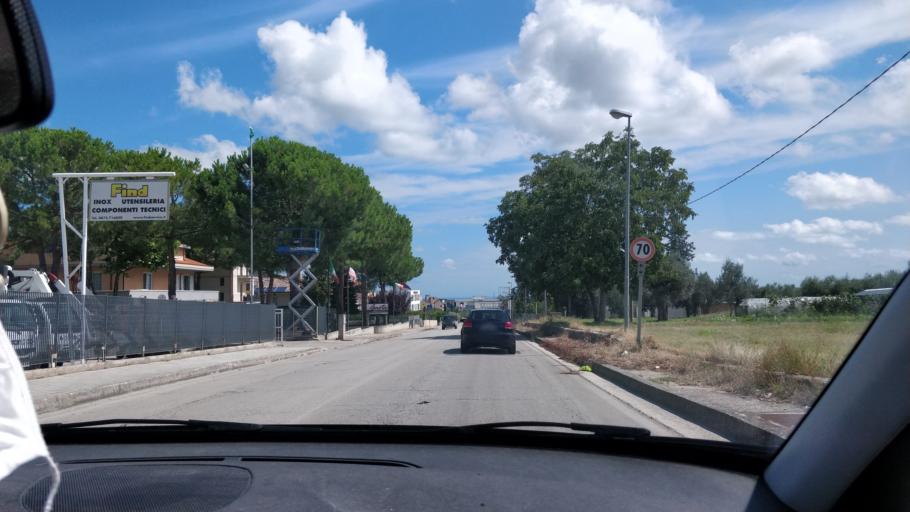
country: IT
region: Abruzzo
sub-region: Provincia di Chieti
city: Treglio
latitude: 42.2504
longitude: 14.4239
